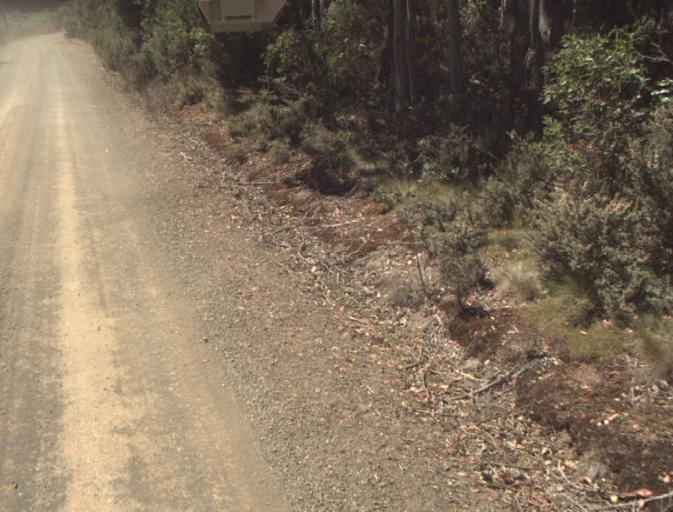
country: AU
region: Tasmania
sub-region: Dorset
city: Scottsdale
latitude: -41.3593
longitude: 147.4188
